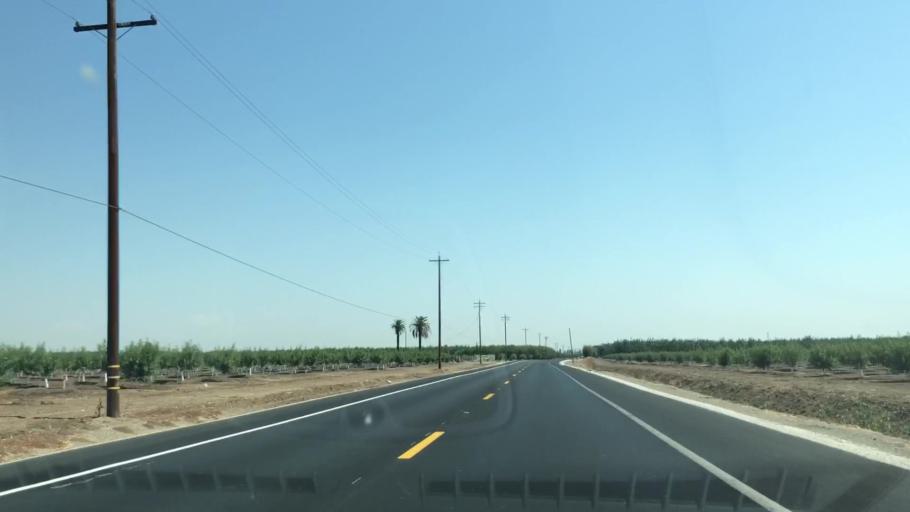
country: US
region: California
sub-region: San Joaquin County
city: Linden
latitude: 37.9345
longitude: -121.0730
